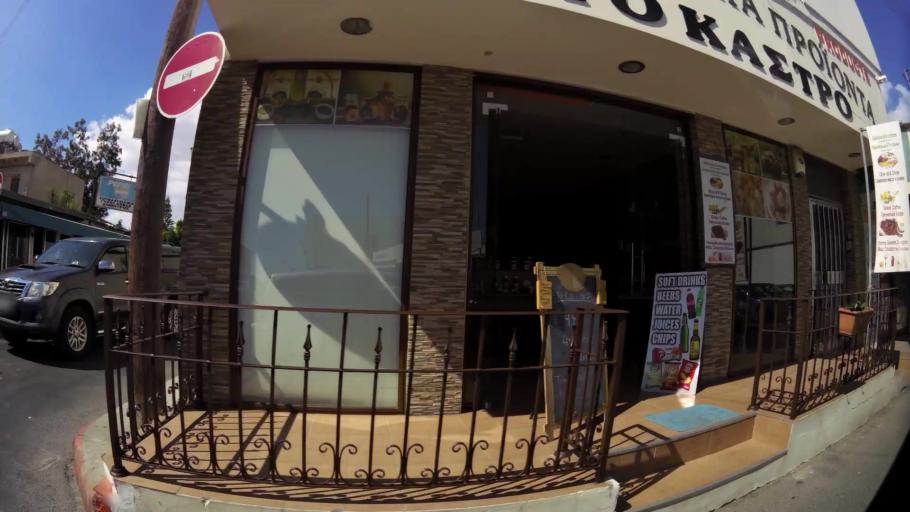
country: CY
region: Larnaka
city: Larnaca
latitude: 34.9108
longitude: 33.6371
